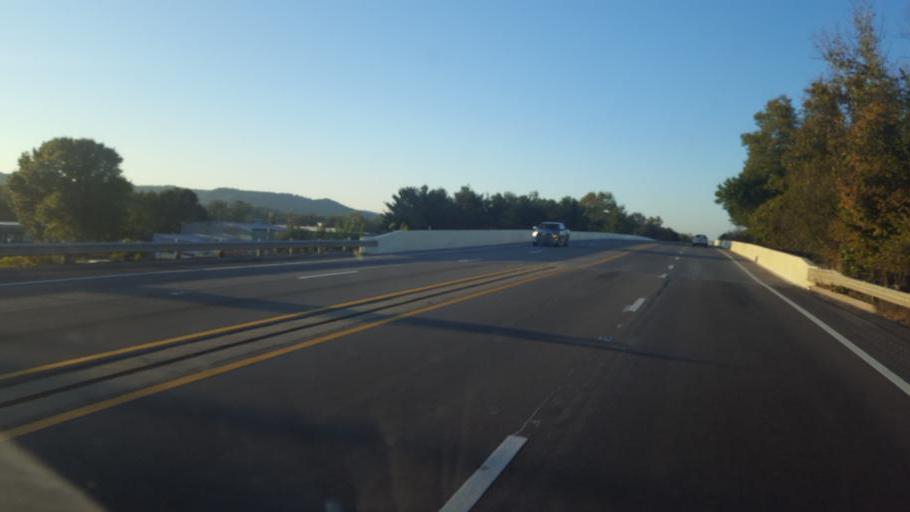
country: US
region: Ohio
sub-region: Scioto County
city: Rosemount
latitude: 38.8040
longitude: -82.9842
